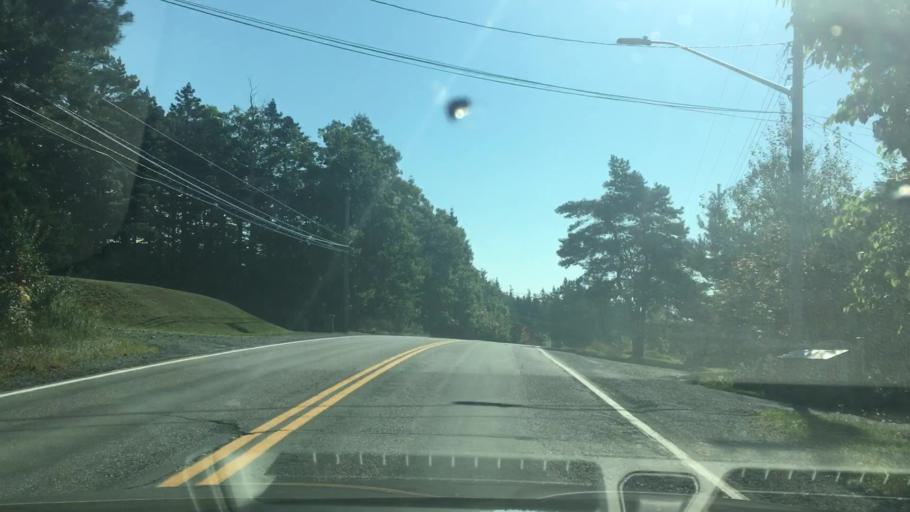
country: CA
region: Nova Scotia
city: Cole Harbour
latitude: 44.7776
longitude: -63.0587
